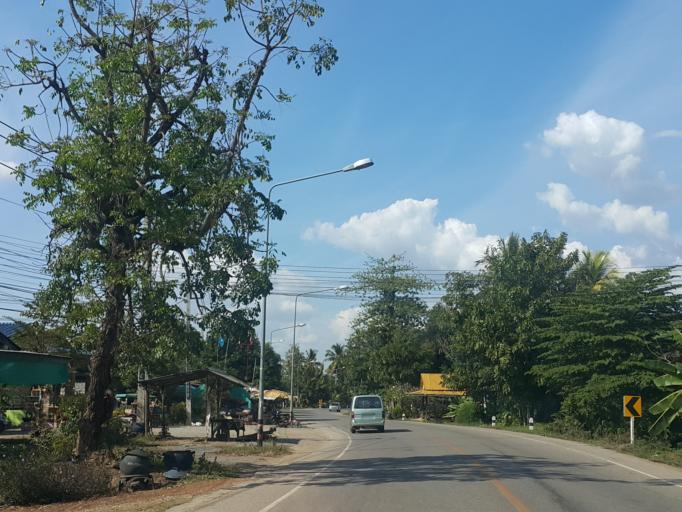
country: TH
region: Sukhothai
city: Sawankhalok
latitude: 17.2948
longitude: 99.8279
